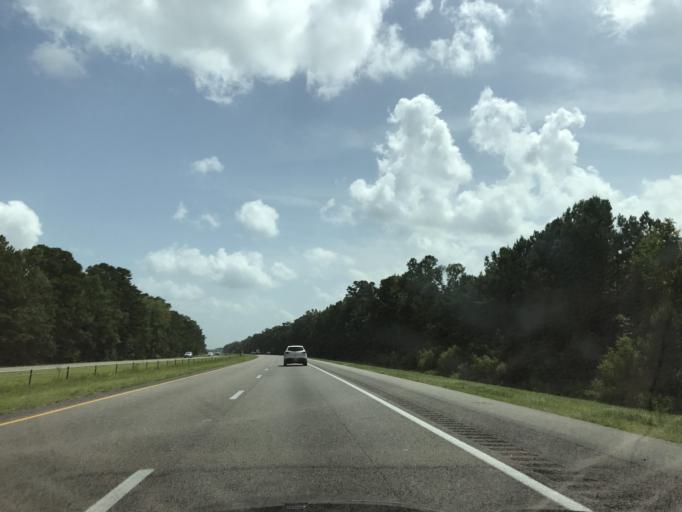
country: US
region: North Carolina
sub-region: Pender County
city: Rocky Point
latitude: 34.4625
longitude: -77.8801
